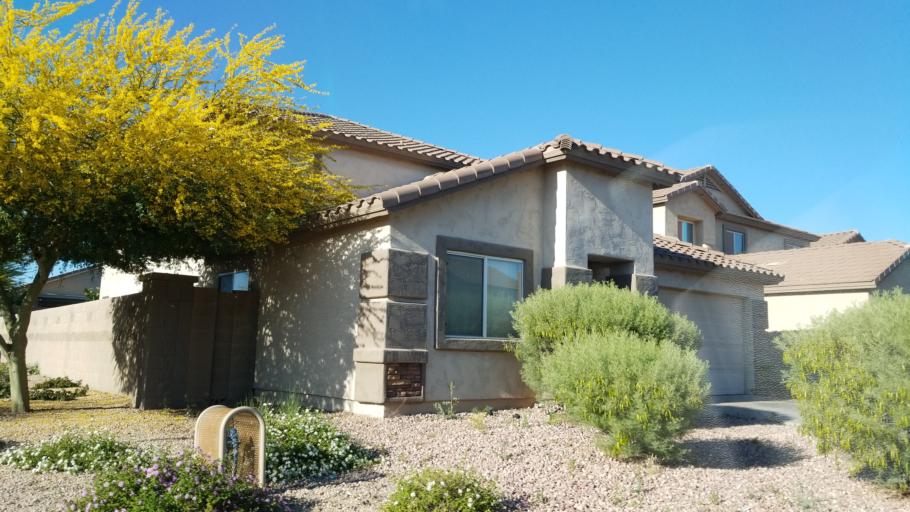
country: US
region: Arizona
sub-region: Maricopa County
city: Youngtown
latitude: 33.5723
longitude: -112.3096
